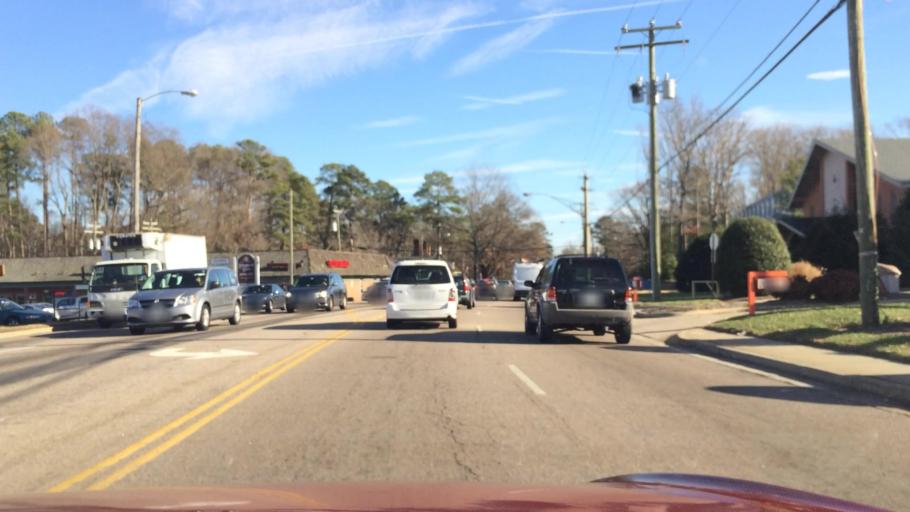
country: US
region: Virginia
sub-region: Chesterfield County
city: Bon Air
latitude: 37.5381
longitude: -77.5198
